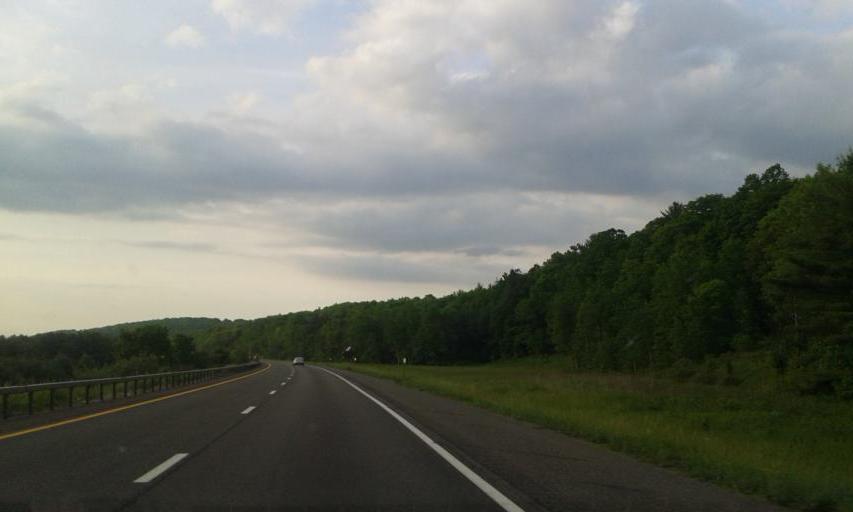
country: US
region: New York
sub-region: Broome County
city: Chenango Bridge
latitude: 42.1984
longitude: -75.8983
